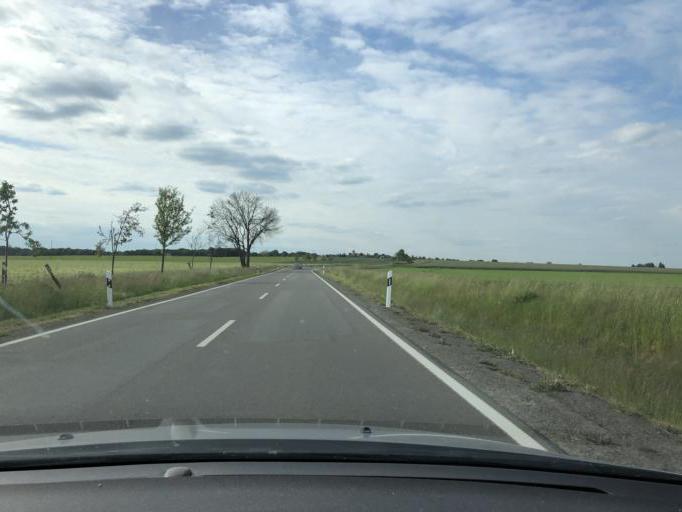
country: DE
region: Saxony
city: Brandis
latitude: 51.3053
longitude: 12.6502
